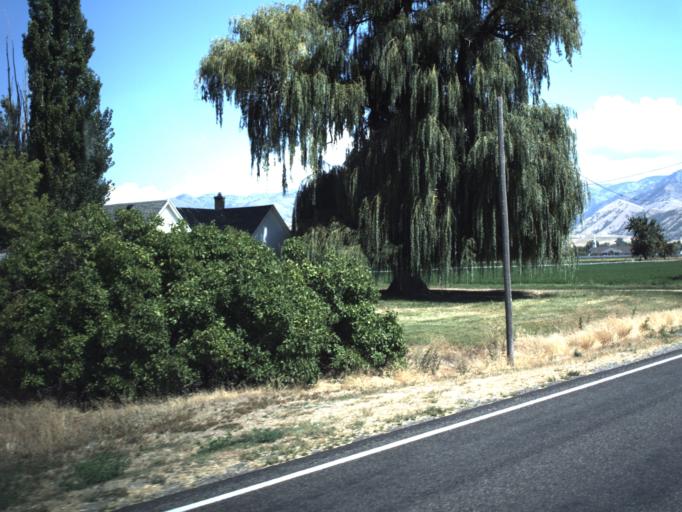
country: US
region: Utah
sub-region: Cache County
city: Smithfield
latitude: 41.8387
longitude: -111.8597
